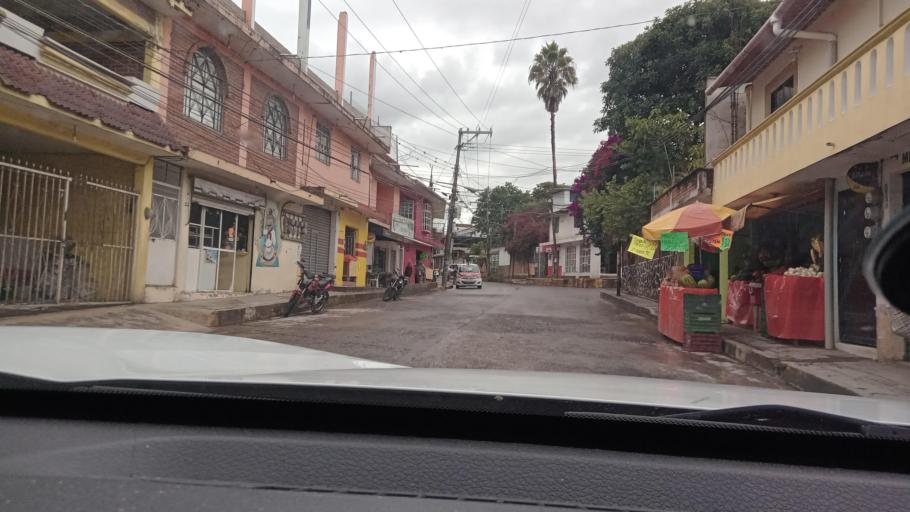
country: MX
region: Veracruz
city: Coatepec
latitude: 19.4473
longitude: -96.9682
